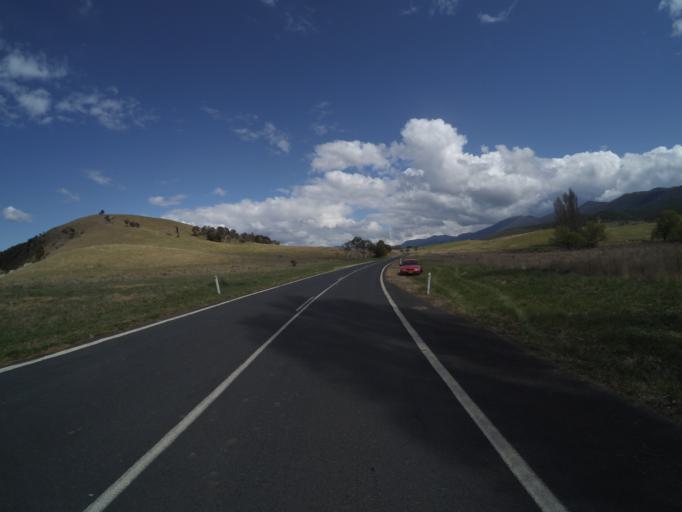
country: AU
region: Australian Capital Territory
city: Macarthur
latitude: -35.4009
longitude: 148.9598
